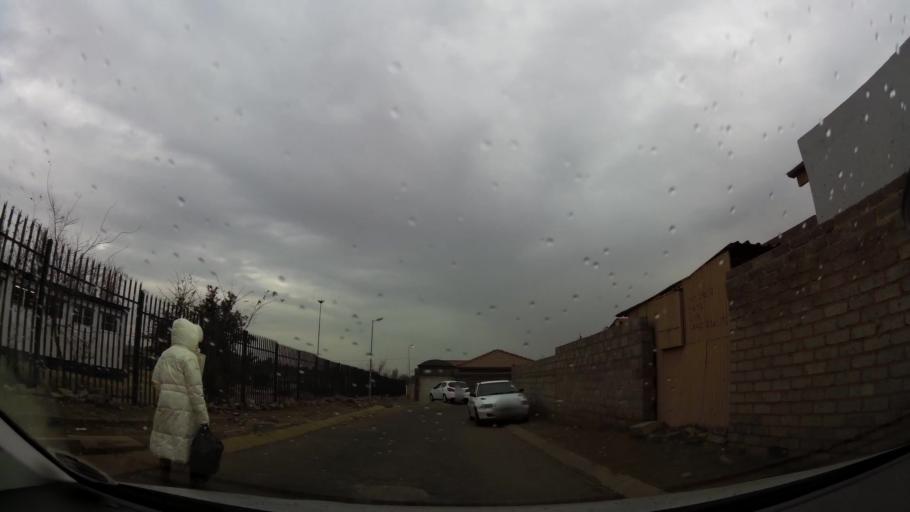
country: ZA
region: Gauteng
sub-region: City of Johannesburg Metropolitan Municipality
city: Soweto
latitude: -26.2524
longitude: 27.8655
